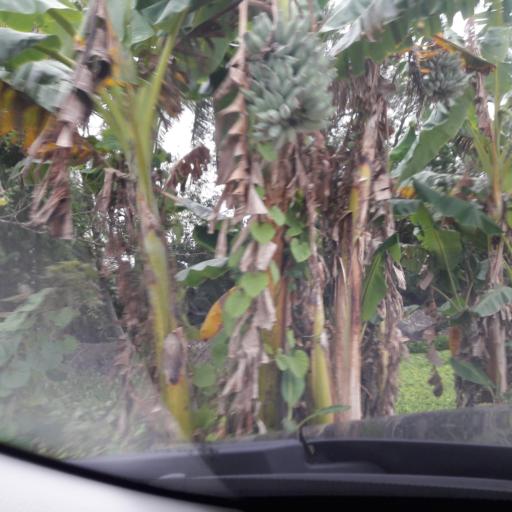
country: TH
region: Ratchaburi
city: Damnoen Saduak
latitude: 13.5747
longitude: 99.9464
